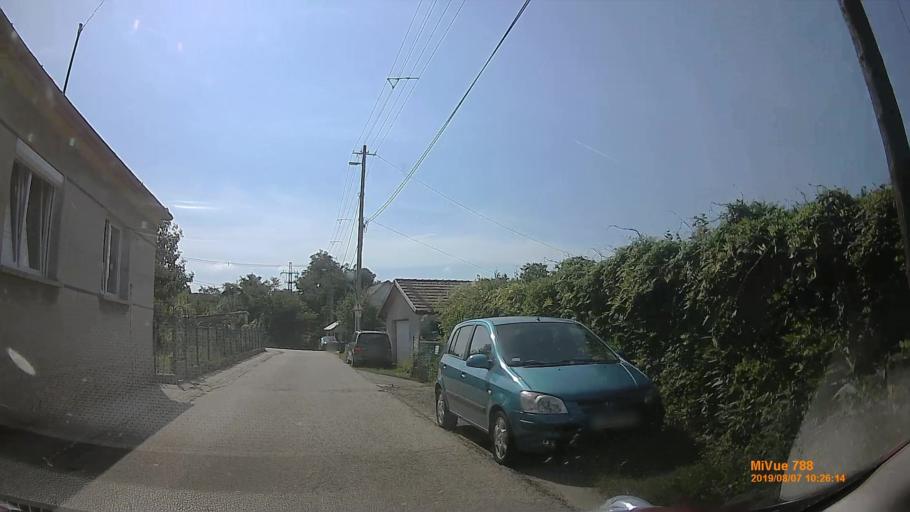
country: HU
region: Veszprem
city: Ajka
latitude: 47.0899
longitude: 17.5650
